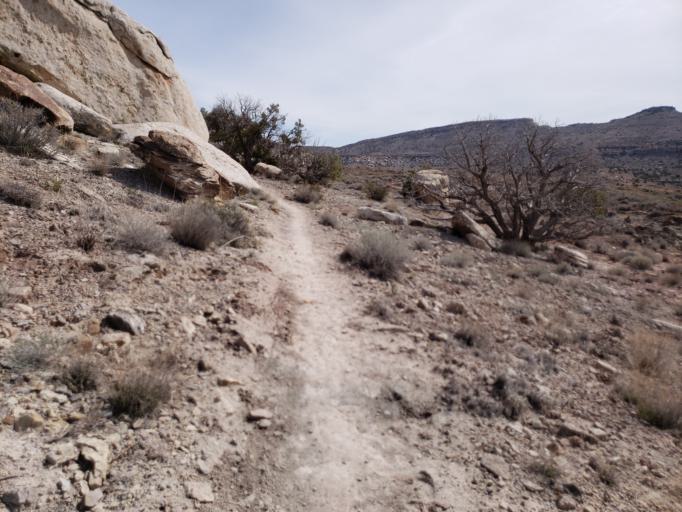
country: US
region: Colorado
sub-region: Mesa County
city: Loma
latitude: 39.1927
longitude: -108.8801
